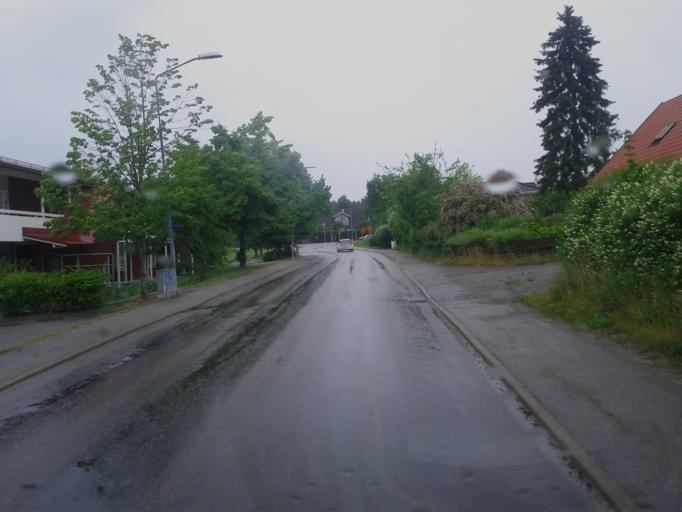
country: SE
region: Stockholm
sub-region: Vallentuna Kommun
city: Vallentuna
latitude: 59.4947
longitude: 18.0634
